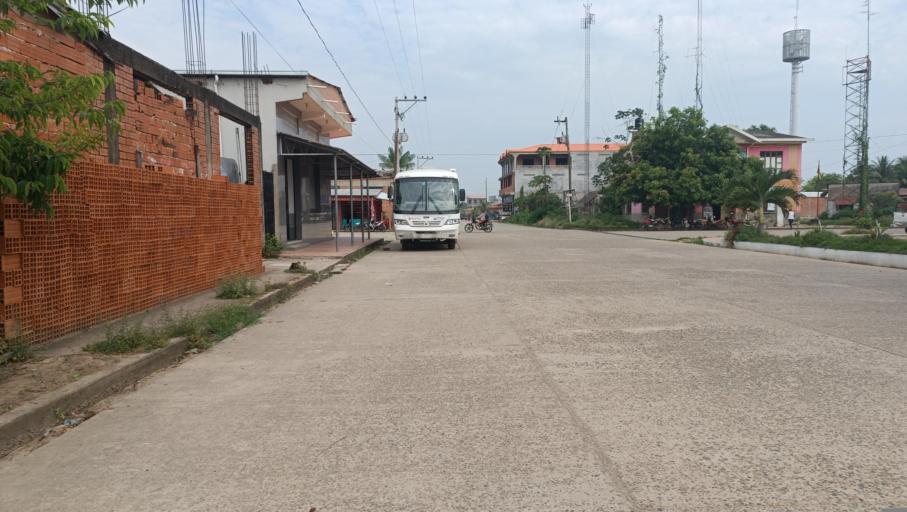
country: BO
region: El Beni
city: Rurrenabaque
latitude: -13.7680
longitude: -68.1263
